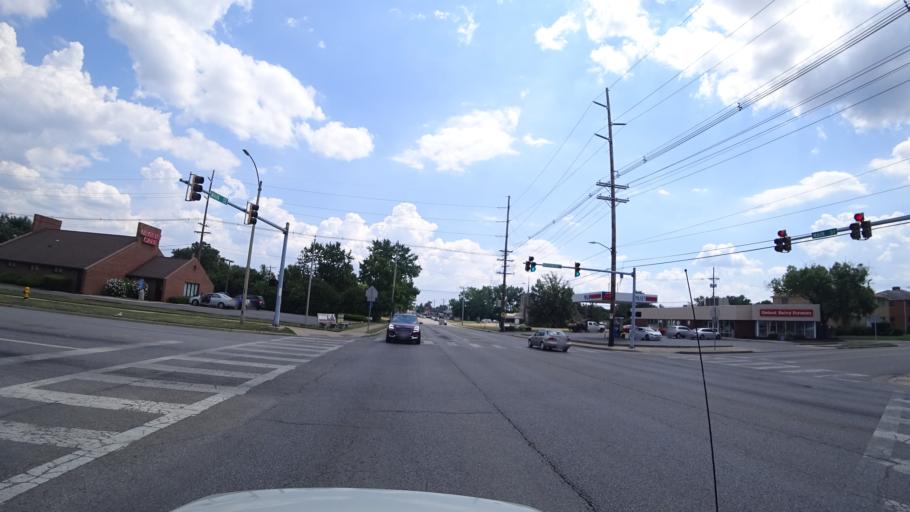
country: US
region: Ohio
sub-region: Butler County
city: Hamilton
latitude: 39.4201
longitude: -84.5895
